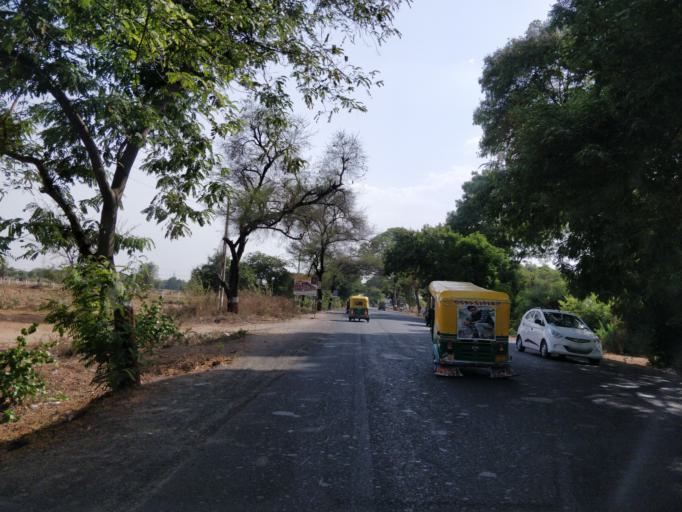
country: IN
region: Gujarat
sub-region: Ahmadabad
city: Naroda
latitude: 23.0952
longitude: 72.6964
